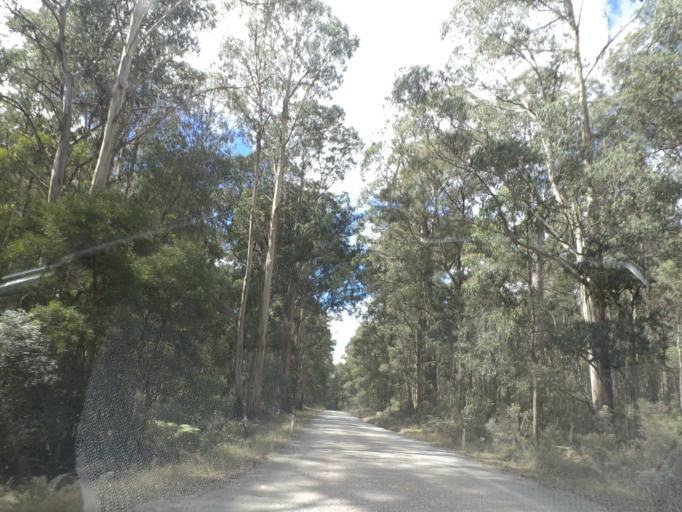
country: AU
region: Victoria
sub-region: Yarra Ranges
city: Millgrove
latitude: -37.5416
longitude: 145.9248
